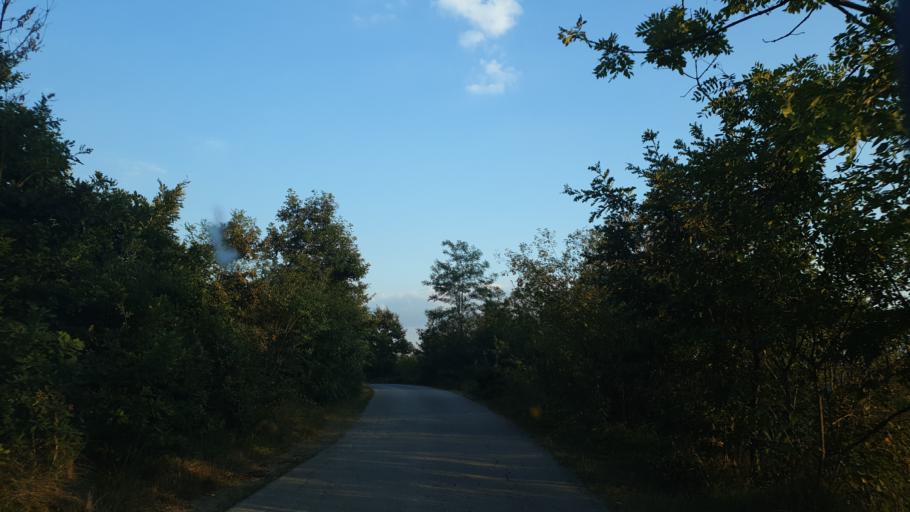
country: RS
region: Central Serbia
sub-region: Zlatiborski Okrug
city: Kosjeric
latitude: 44.0259
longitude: 20.0087
